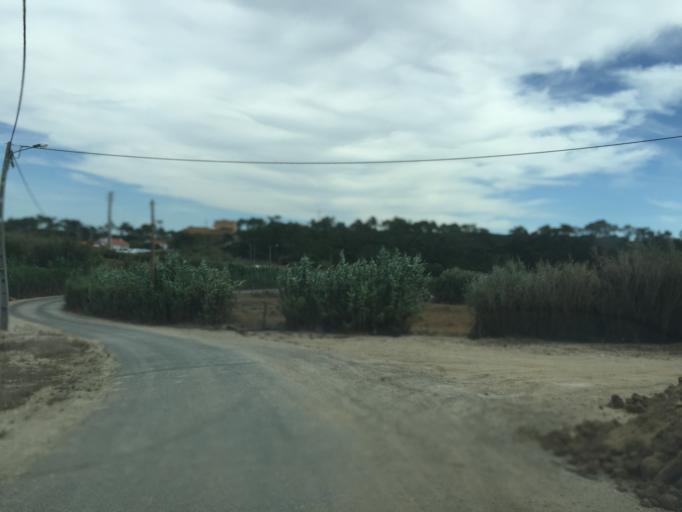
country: PT
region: Lisbon
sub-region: Lourinha
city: Lourinha
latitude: 39.1859
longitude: -9.3414
